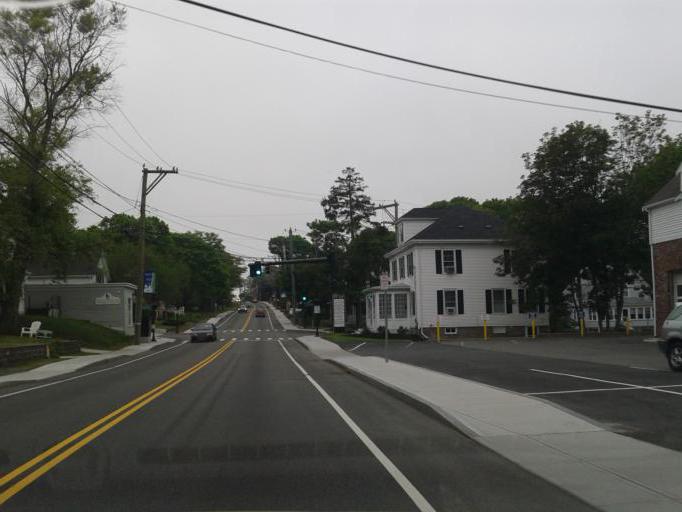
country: US
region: Massachusetts
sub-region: Plymouth County
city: Plymouth
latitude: 41.9575
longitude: -70.6746
